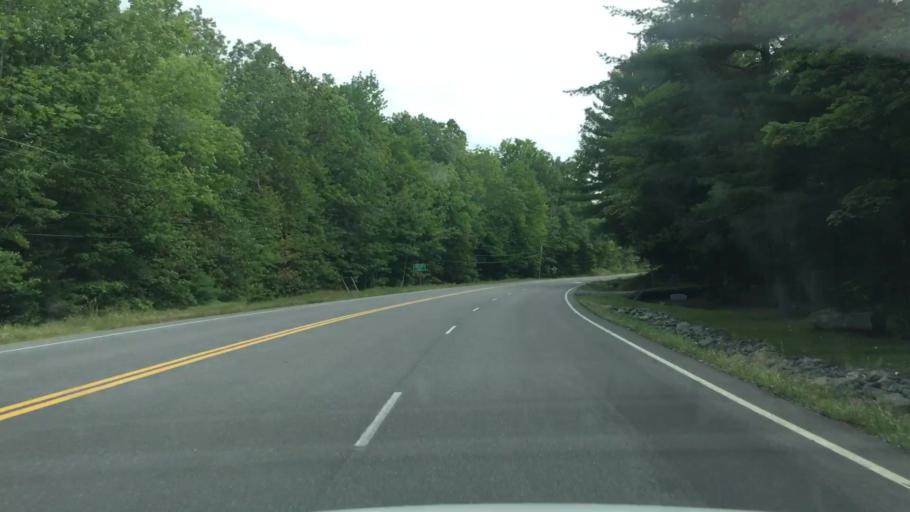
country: US
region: Maine
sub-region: Piscataquis County
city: Dover-Foxcroft
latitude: 45.2143
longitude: -69.1683
